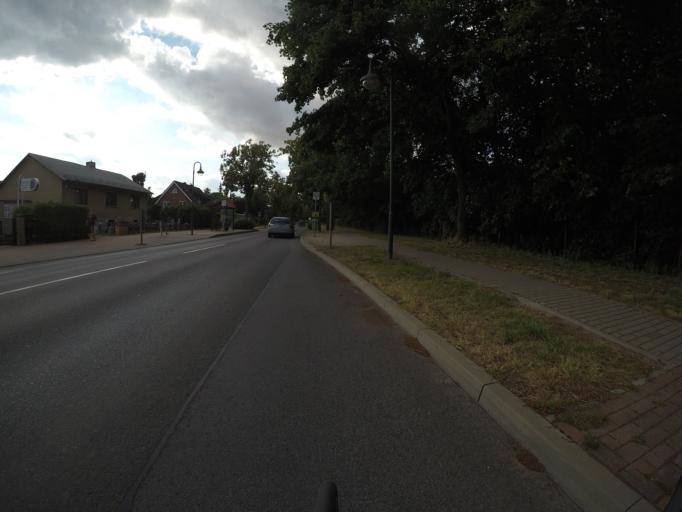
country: DE
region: Brandenburg
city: Ahrensfelde
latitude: 52.5798
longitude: 13.5712
